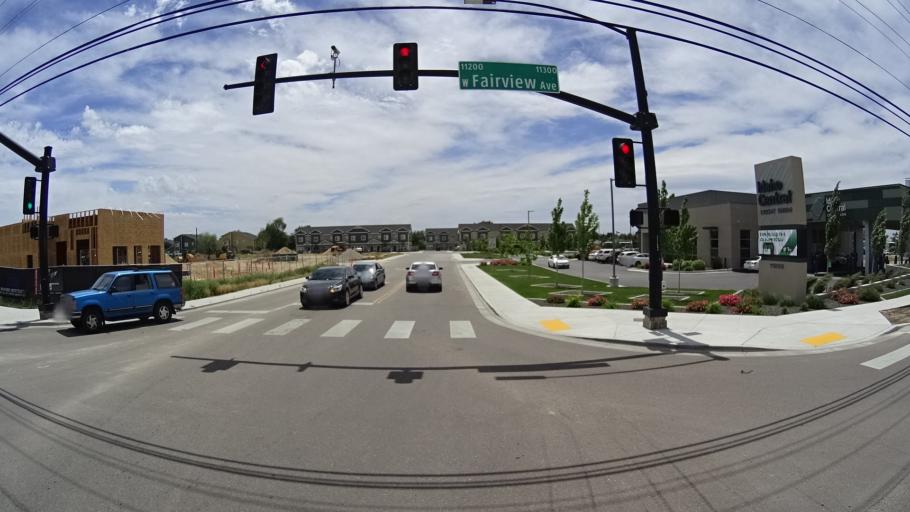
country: US
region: Idaho
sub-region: Ada County
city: Meridian
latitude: 43.6194
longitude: -116.3227
